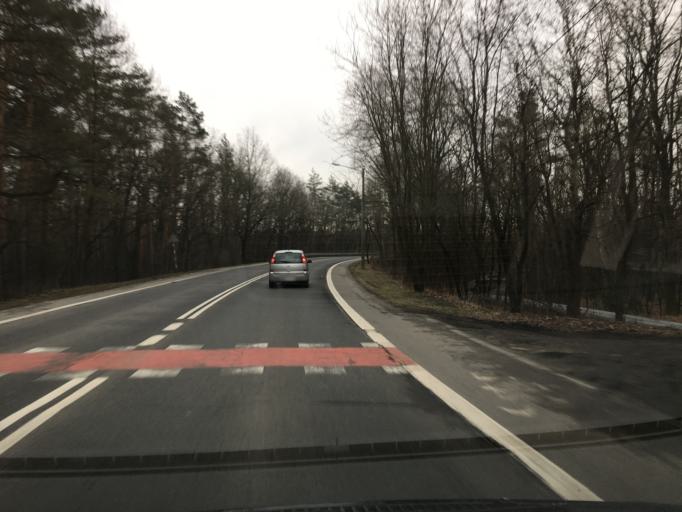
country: PL
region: Opole Voivodeship
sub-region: Powiat kedzierzynsko-kozielski
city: Kedzierzyn-Kozle
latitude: 50.3386
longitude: 18.2346
